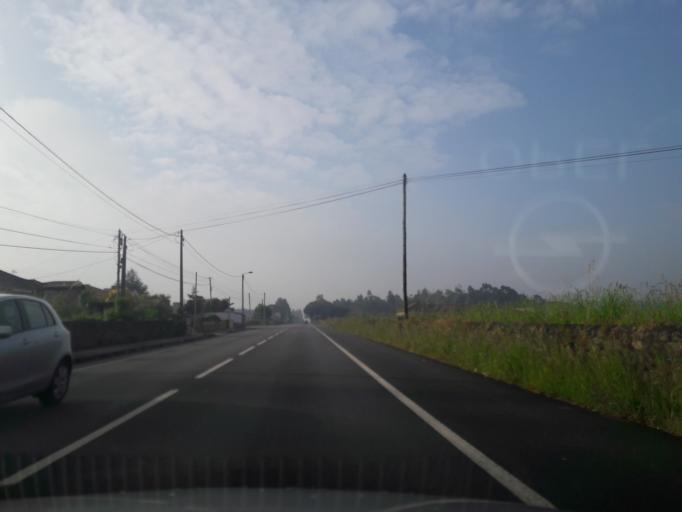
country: PT
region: Porto
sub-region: Vila do Conde
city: Arvore
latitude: 41.3121
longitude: -8.7071
